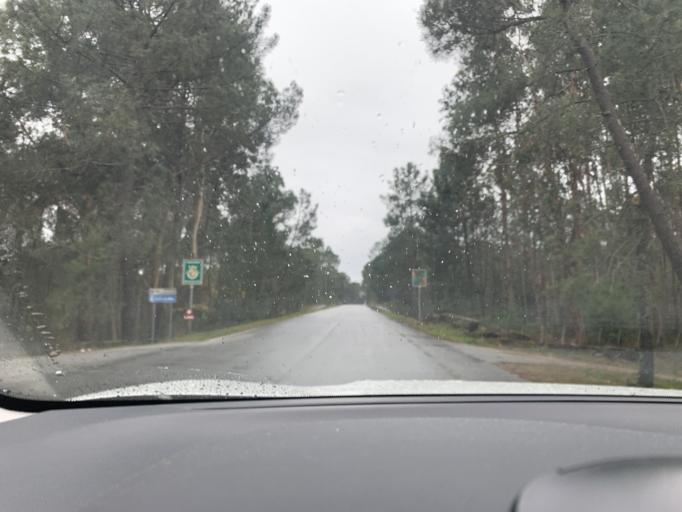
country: PT
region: Viseu
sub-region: Nelas
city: Nelas
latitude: 40.5938
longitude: -7.8302
